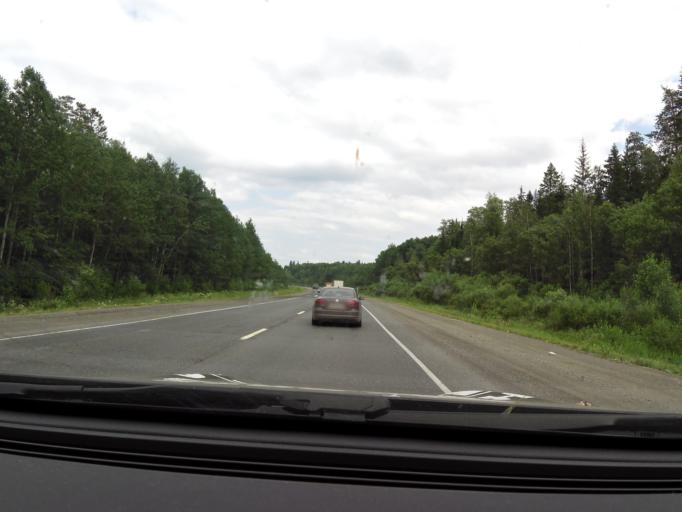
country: RU
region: Sverdlovsk
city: Bilimbay
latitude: 56.8586
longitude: 59.7369
